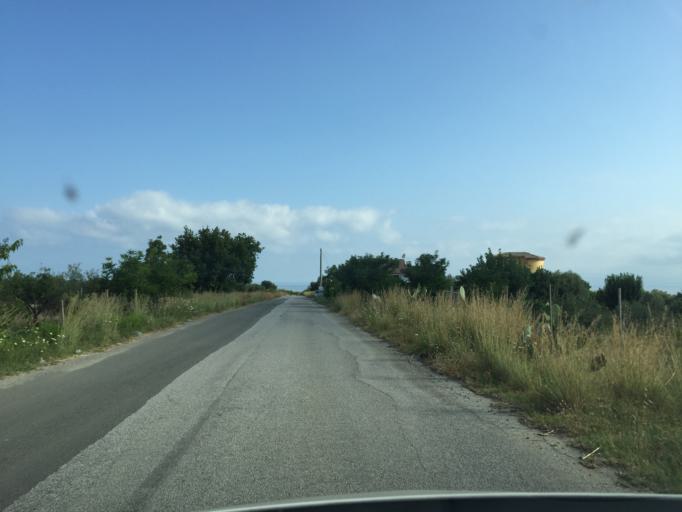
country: IT
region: Calabria
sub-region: Provincia di Vibo-Valentia
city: Pannaconi
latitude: 38.7115
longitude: 16.0491
